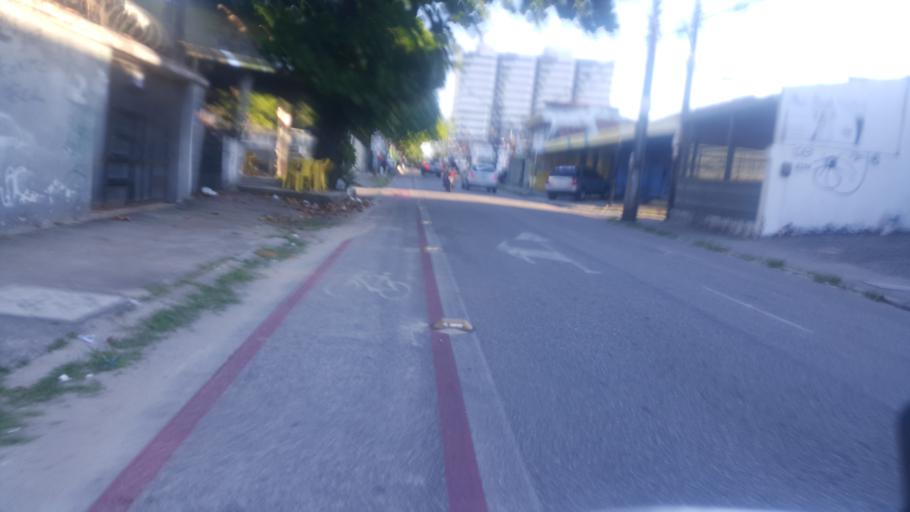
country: BR
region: Ceara
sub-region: Fortaleza
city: Fortaleza
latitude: -3.7371
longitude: -38.5327
